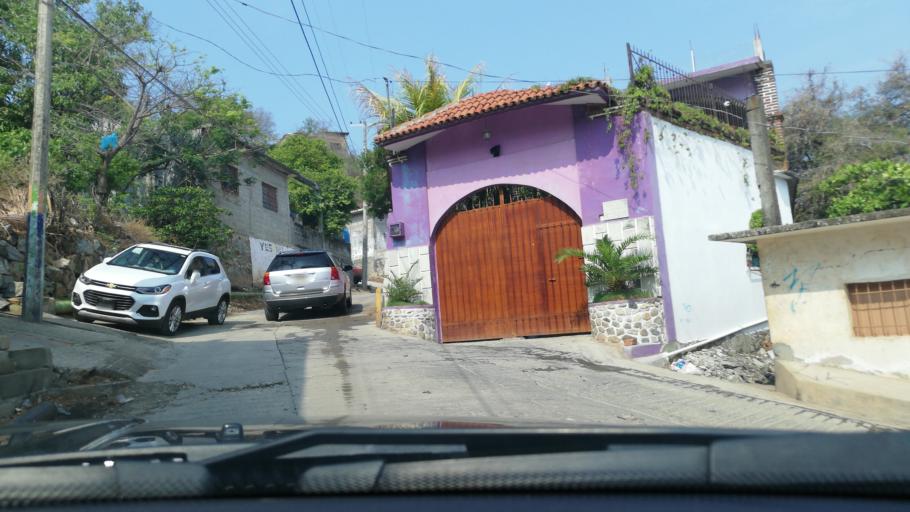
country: MX
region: Oaxaca
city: San Blas Atempa
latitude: 16.3345
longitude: -95.2250
